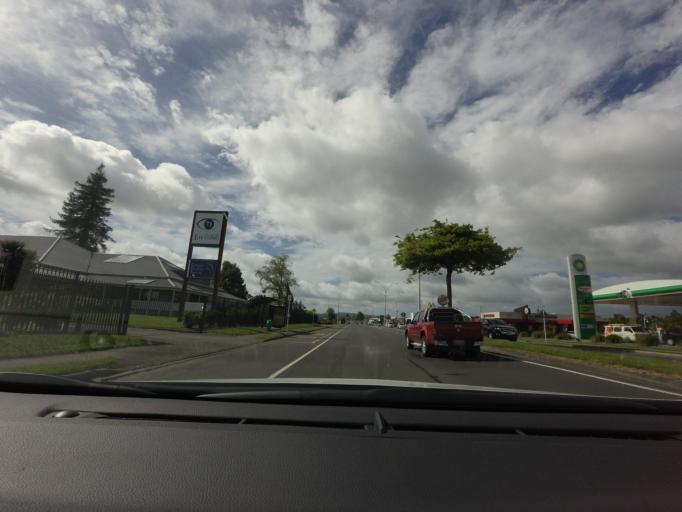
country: NZ
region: Bay of Plenty
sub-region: Rotorua District
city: Rotorua
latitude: -38.1175
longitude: 176.2273
